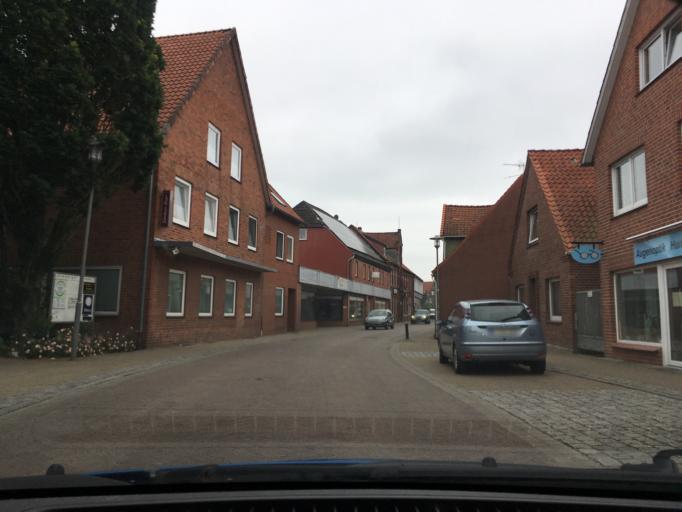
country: DE
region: Lower Saxony
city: Dahlenburg
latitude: 53.1875
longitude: 10.7402
